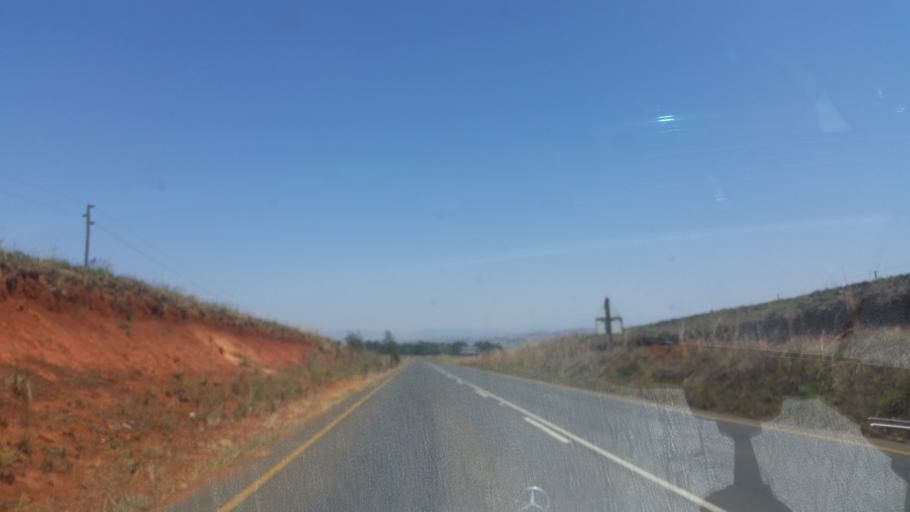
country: ZA
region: KwaZulu-Natal
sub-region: uMgungundlovu District Municipality
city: Mooirivier
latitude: -29.1436
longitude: 29.9934
